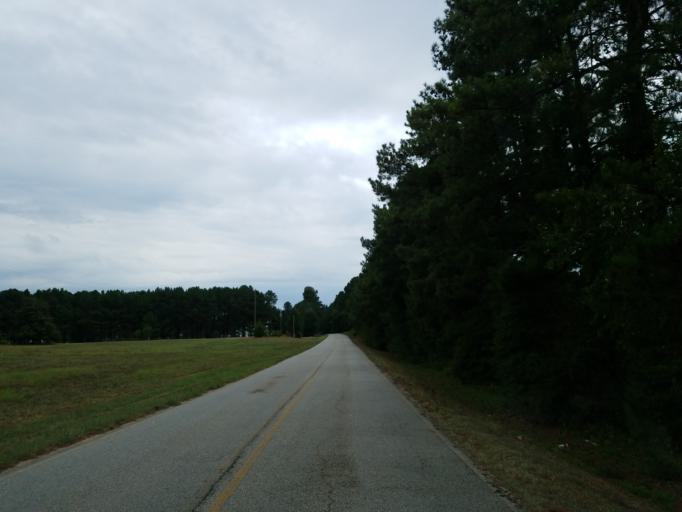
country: US
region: Georgia
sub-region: Clayton County
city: Lovejoy
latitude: 33.4255
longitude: -84.3118
